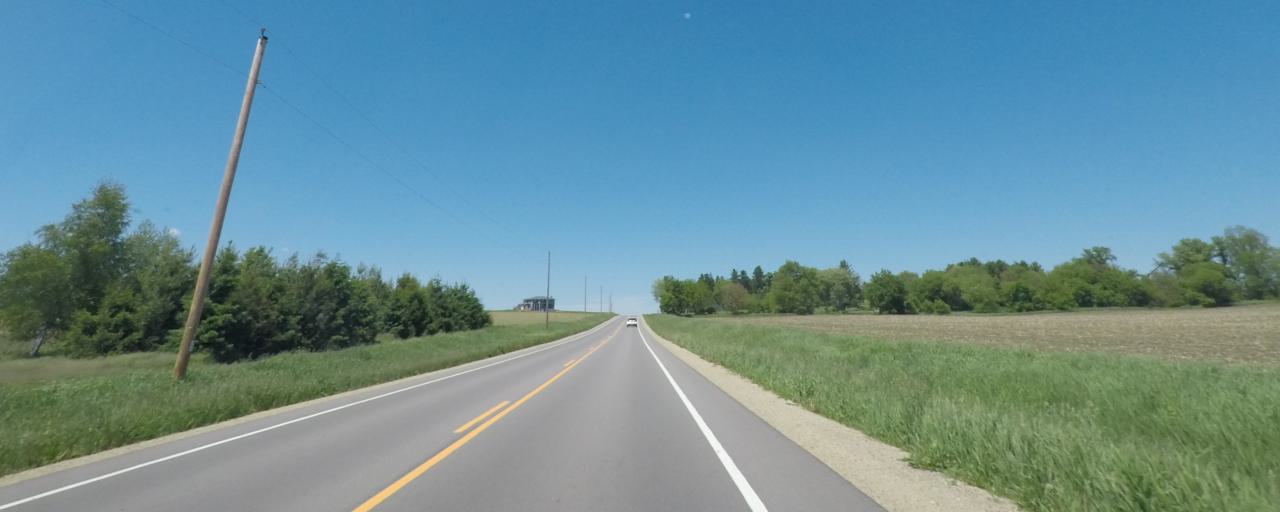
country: US
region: Wisconsin
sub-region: Green County
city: Brooklyn
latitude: 42.8212
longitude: -89.3692
